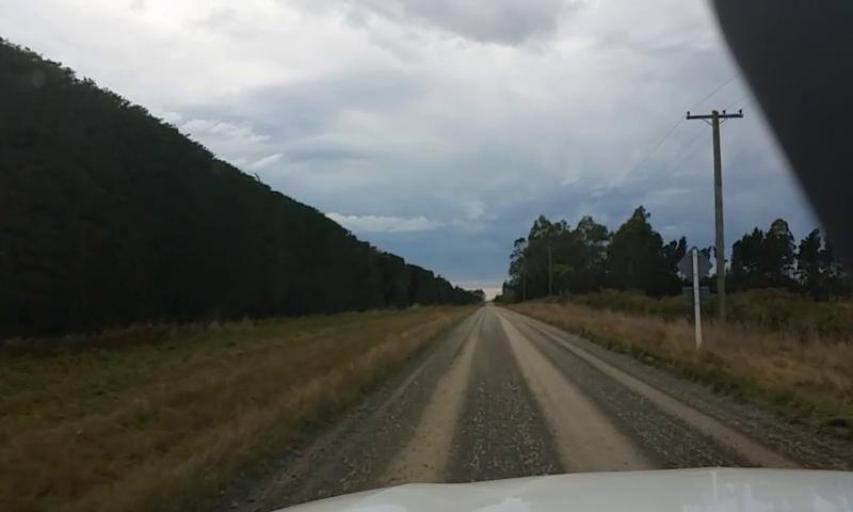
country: NZ
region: Canterbury
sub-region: Waimakariri District
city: Kaiapoi
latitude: -43.2914
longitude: 172.4483
